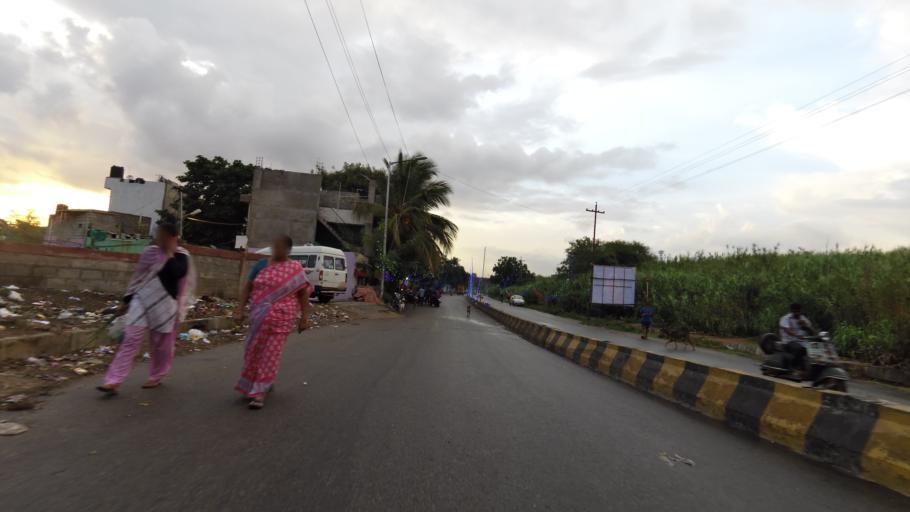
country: IN
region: Karnataka
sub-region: Bangalore Urban
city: Bangalore
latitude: 12.9981
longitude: 77.6411
